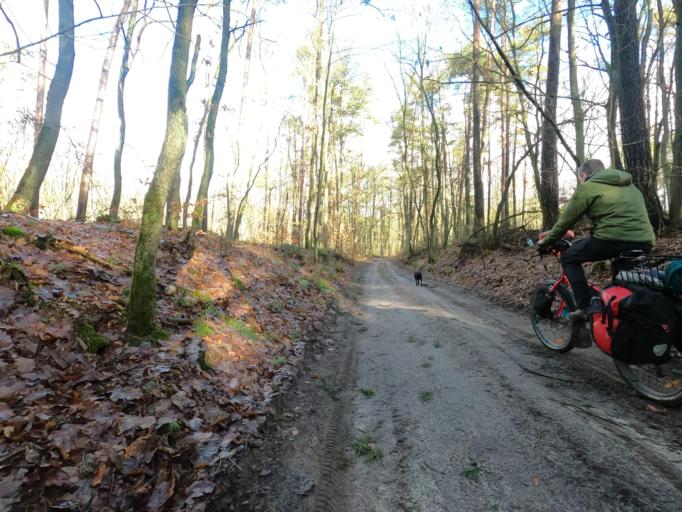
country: PL
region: Greater Poland Voivodeship
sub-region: Powiat pilski
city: Smilowo
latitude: 53.1124
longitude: 16.9492
